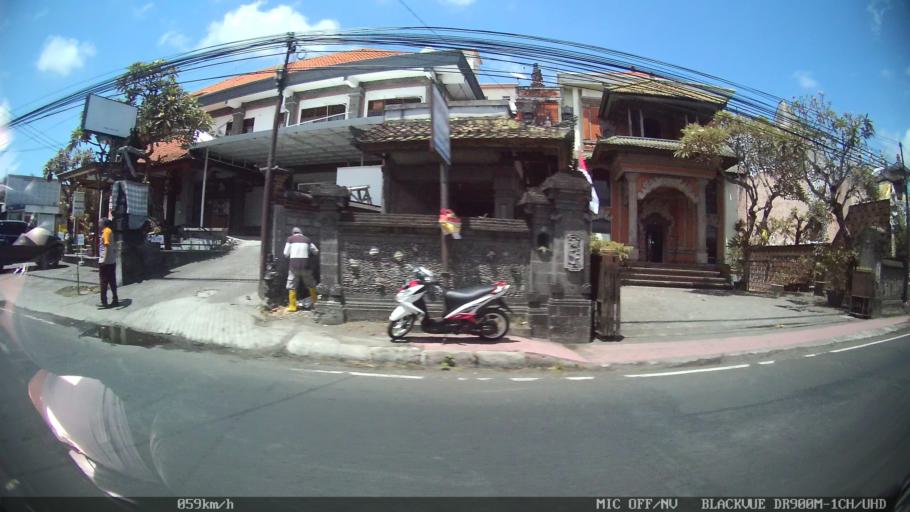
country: ID
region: Bali
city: Banjar Jabejero
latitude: -8.6022
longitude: 115.2638
